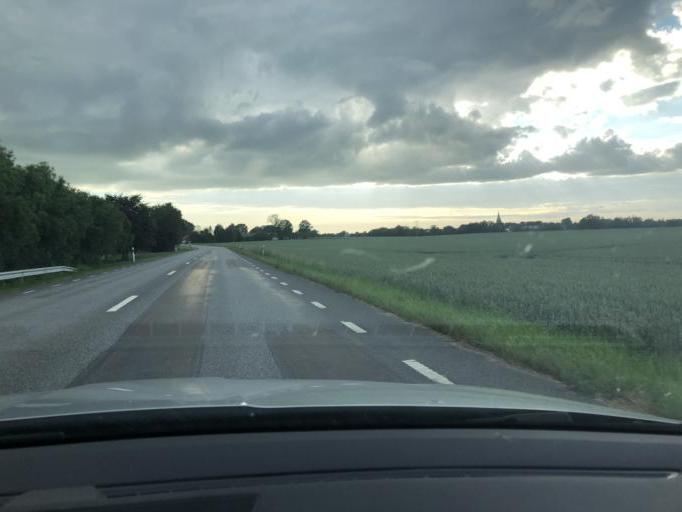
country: SE
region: Skane
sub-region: Simrishamns Kommun
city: Simrishamn
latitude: 55.5290
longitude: 14.2539
